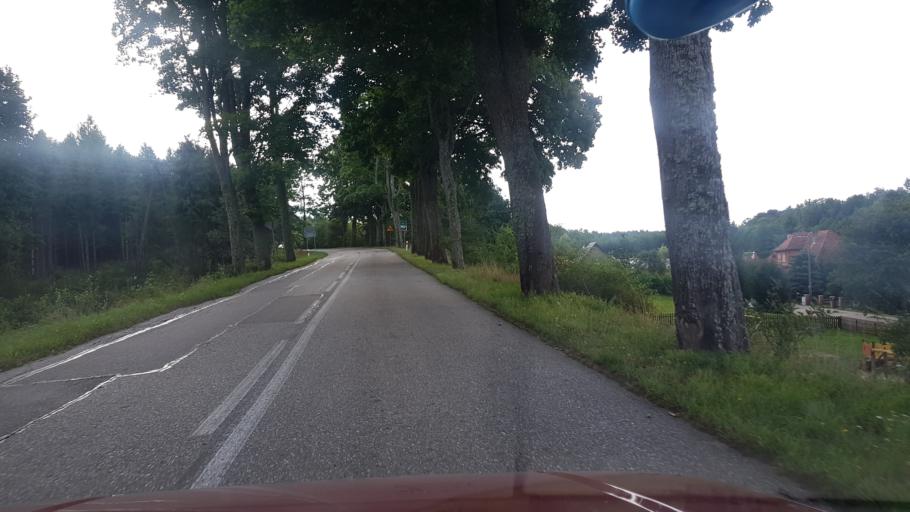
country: PL
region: West Pomeranian Voivodeship
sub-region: Powiat koszalinski
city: Polanow
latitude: 54.0905
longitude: 16.8341
